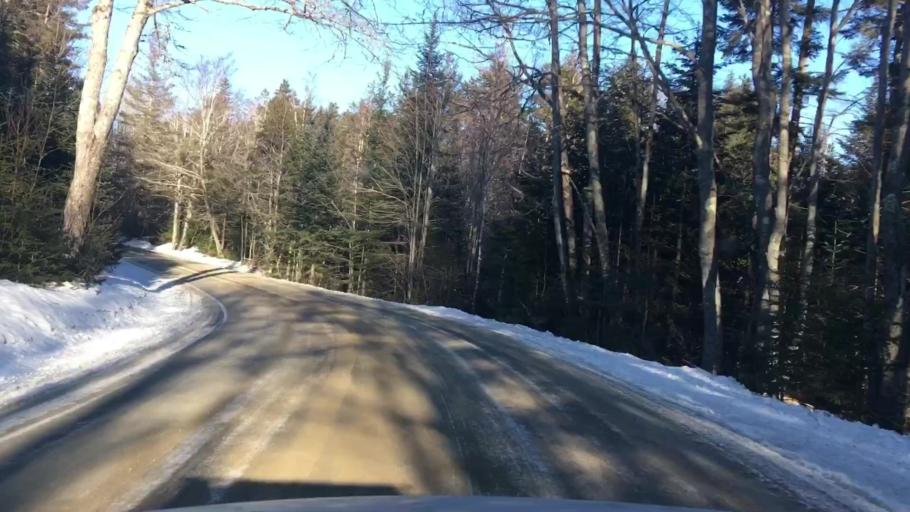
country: US
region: Maine
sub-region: Hancock County
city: Castine
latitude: 44.3833
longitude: -68.7457
